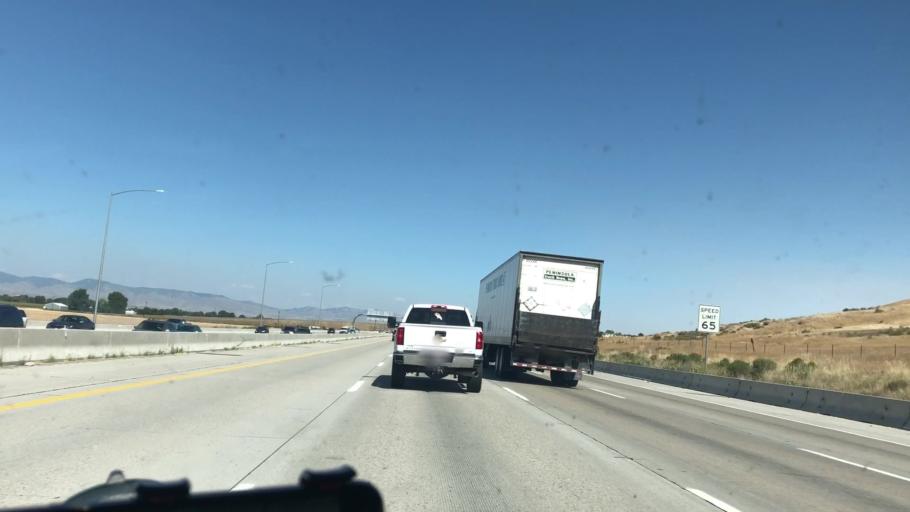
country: US
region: Idaho
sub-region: Canyon County
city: Nampa
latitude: 43.5995
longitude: -116.5022
